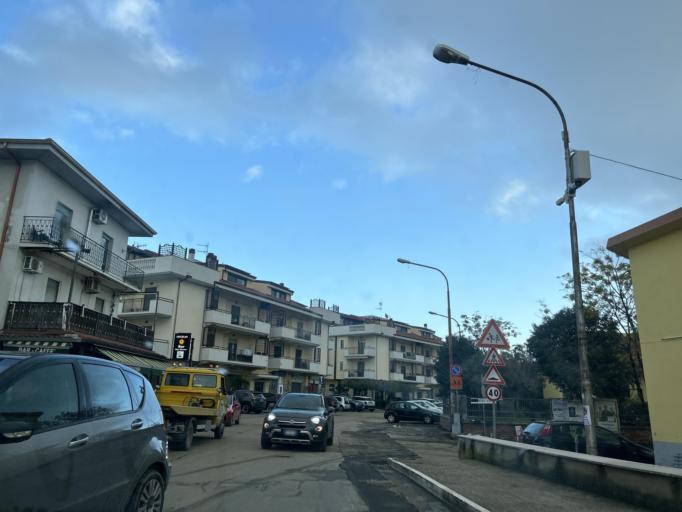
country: IT
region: Calabria
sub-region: Provincia di Catanzaro
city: Squillace Lido
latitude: 38.7793
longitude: 16.5685
